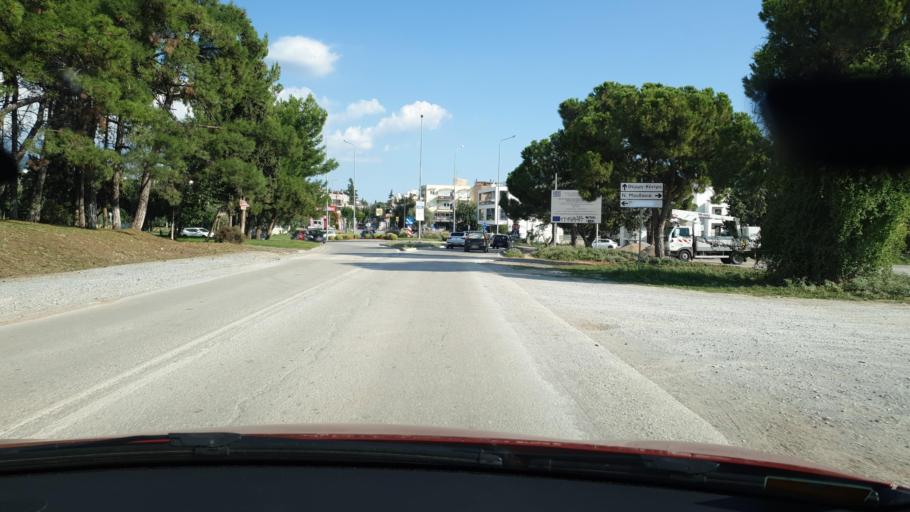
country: GR
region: Central Macedonia
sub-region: Nomos Thessalonikis
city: Thermi
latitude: 40.5535
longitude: 23.0164
